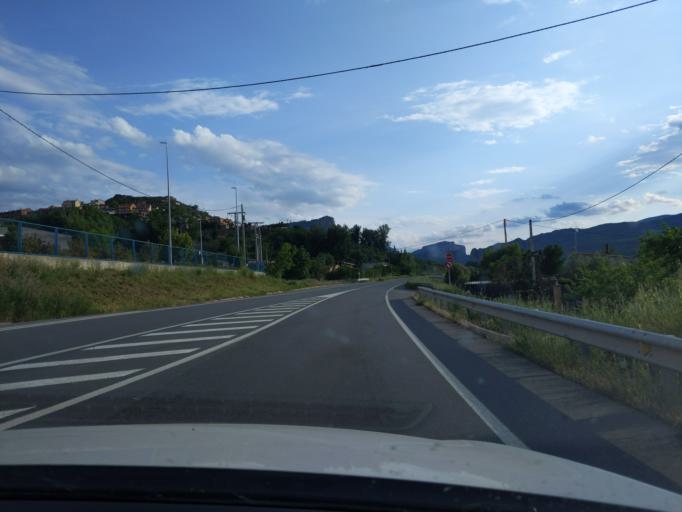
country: ES
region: La Rioja
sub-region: Provincia de La Rioja
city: Nalda
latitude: 42.3404
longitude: -2.4858
